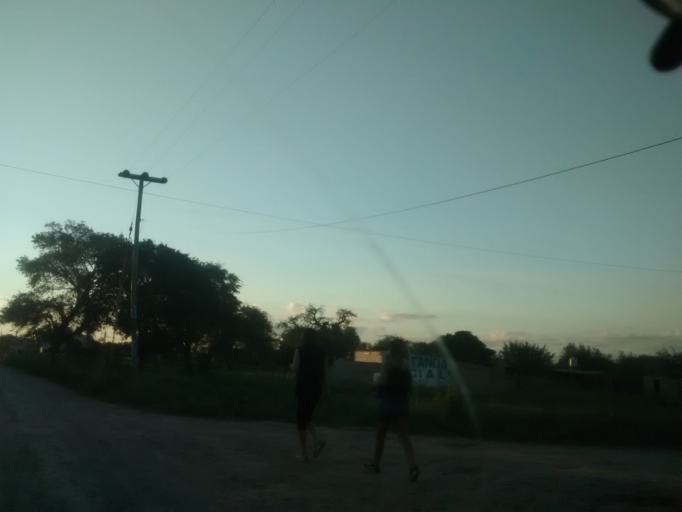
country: AR
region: Chaco
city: Fontana
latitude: -27.4021
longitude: -58.9929
